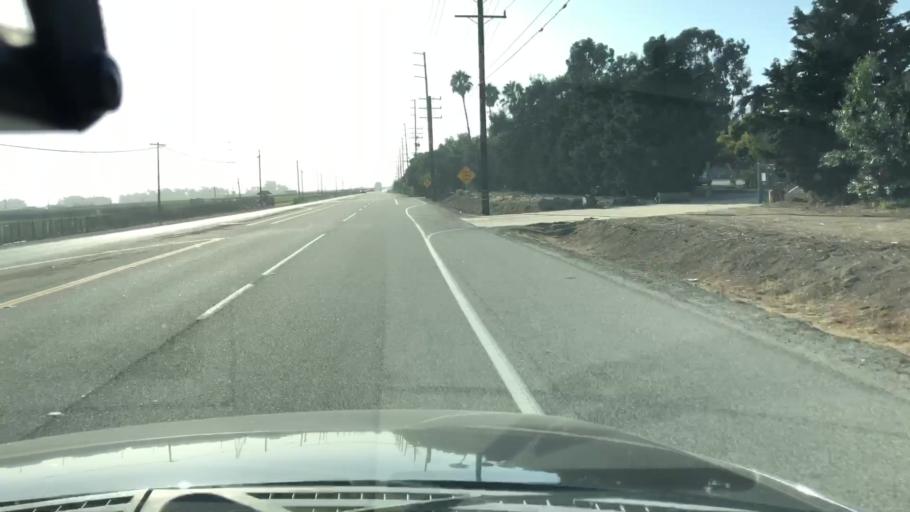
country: US
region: California
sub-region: Ventura County
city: Oxnard Shores
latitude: 34.2195
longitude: -119.2236
